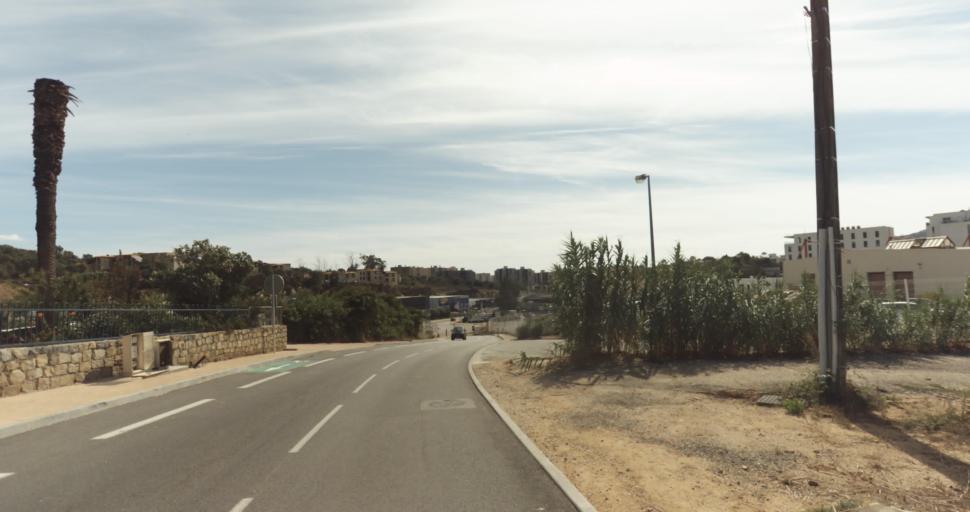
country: FR
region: Corsica
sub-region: Departement de la Corse-du-Sud
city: Ajaccio
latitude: 41.9463
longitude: 8.7583
